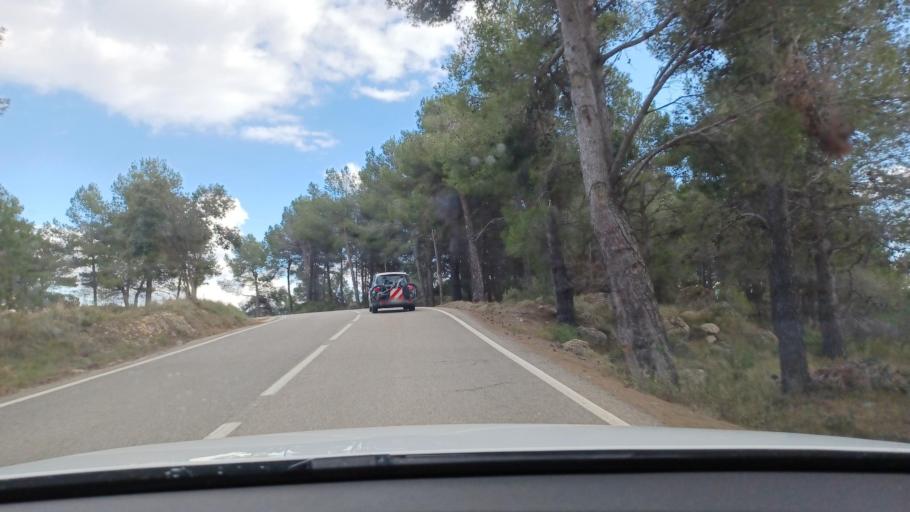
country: ES
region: Catalonia
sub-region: Provincia de Tarragona
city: la Morera de Montsant
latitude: 41.2677
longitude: 0.8650
